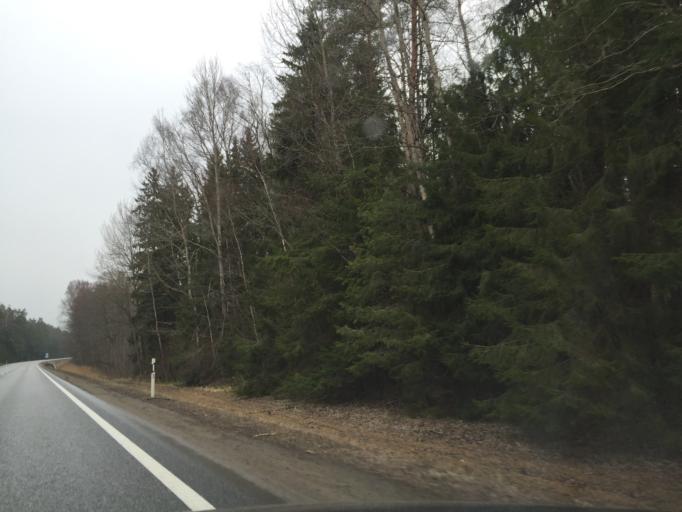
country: LV
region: Saulkrastu
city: Saulkrasti
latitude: 57.5014
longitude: 24.4306
